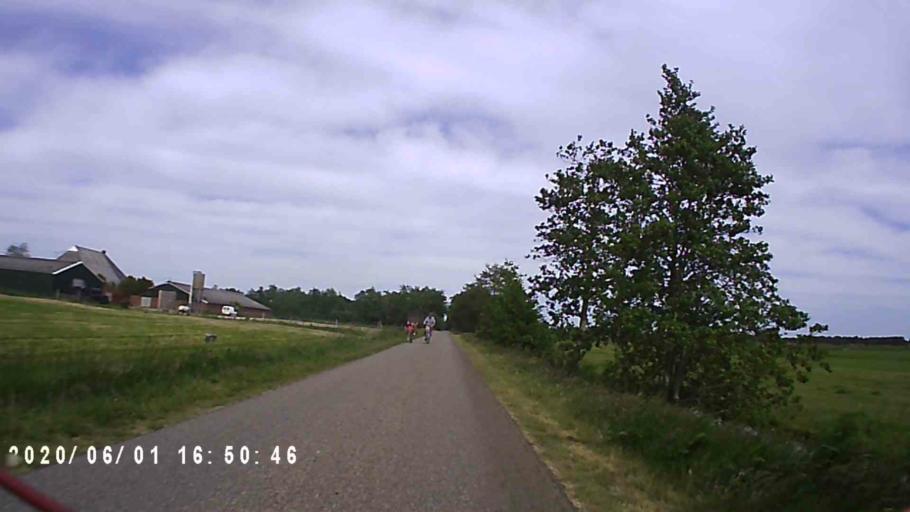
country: NL
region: Friesland
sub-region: Gemeente Tytsjerksteradiel
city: Tytsjerk
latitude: 53.1879
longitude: 5.9127
